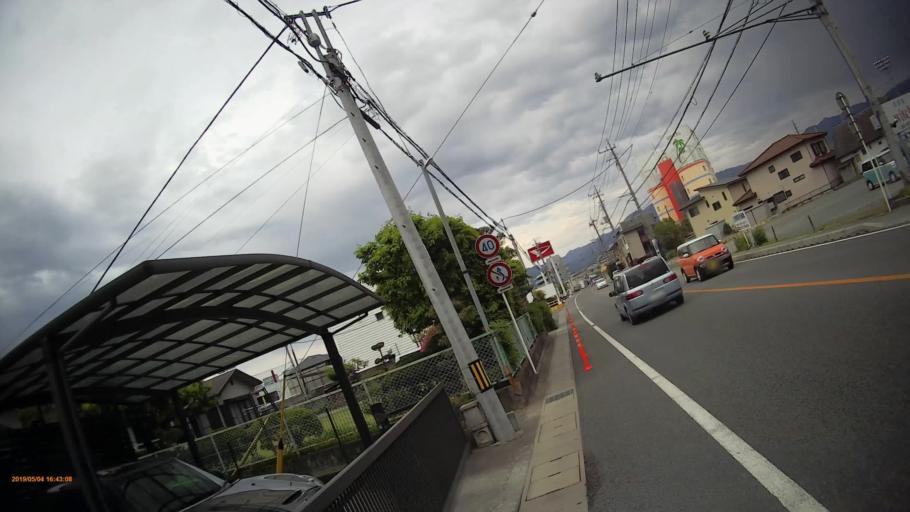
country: JP
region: Yamanashi
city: Isawa
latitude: 35.6559
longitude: 138.6068
